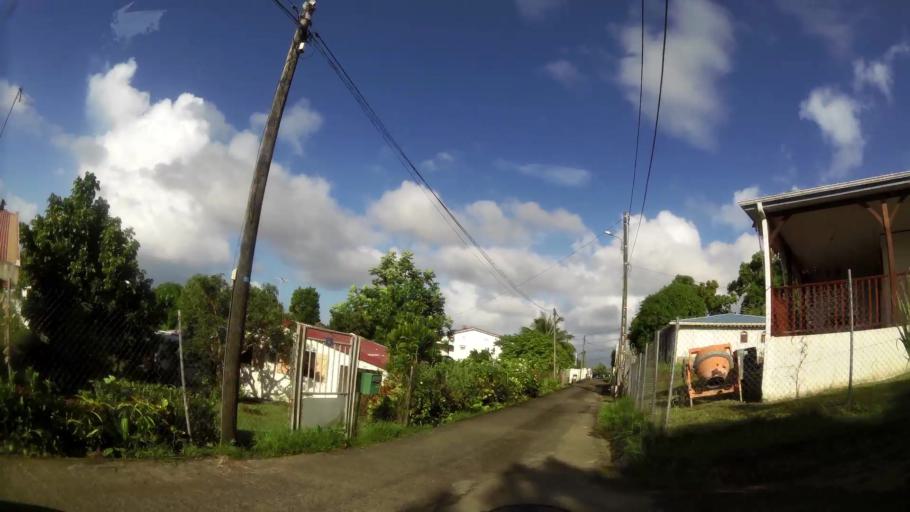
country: MQ
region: Martinique
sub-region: Martinique
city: Ducos
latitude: 14.5739
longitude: -60.9654
